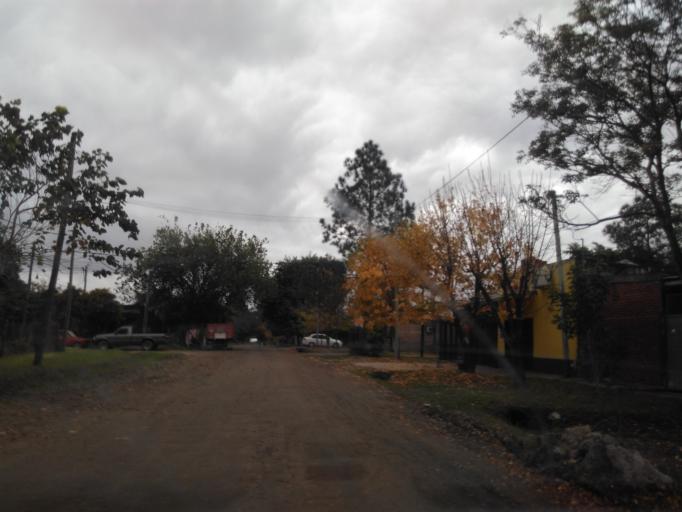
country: AR
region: Chaco
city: Fontana
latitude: -27.4309
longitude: -59.0159
